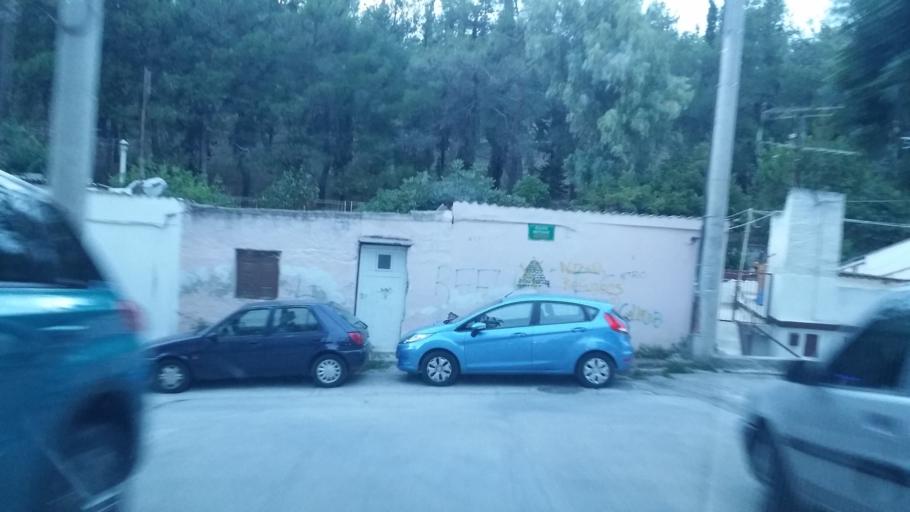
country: GR
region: Attica
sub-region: Nomarchia Athinas
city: Nea Ionia
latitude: 38.0440
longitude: 23.7479
